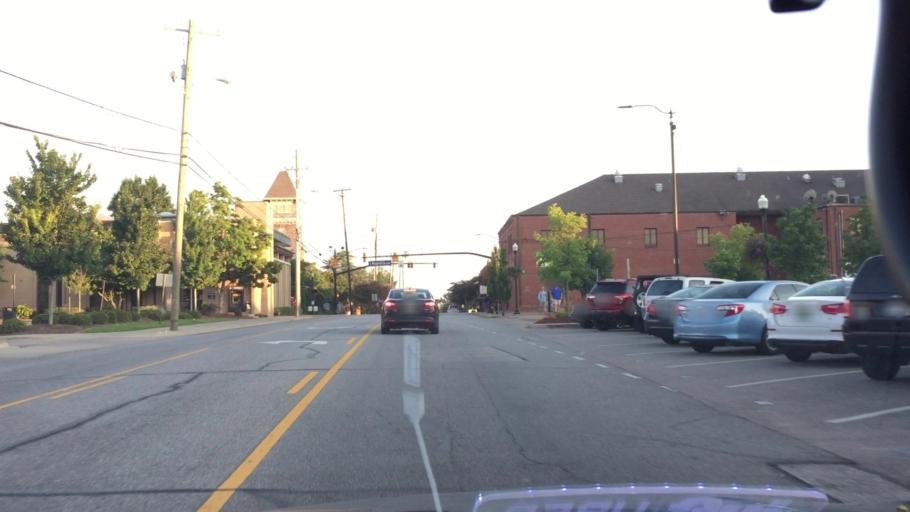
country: US
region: Alabama
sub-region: Lee County
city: Auburn
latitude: 32.6075
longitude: -85.4799
